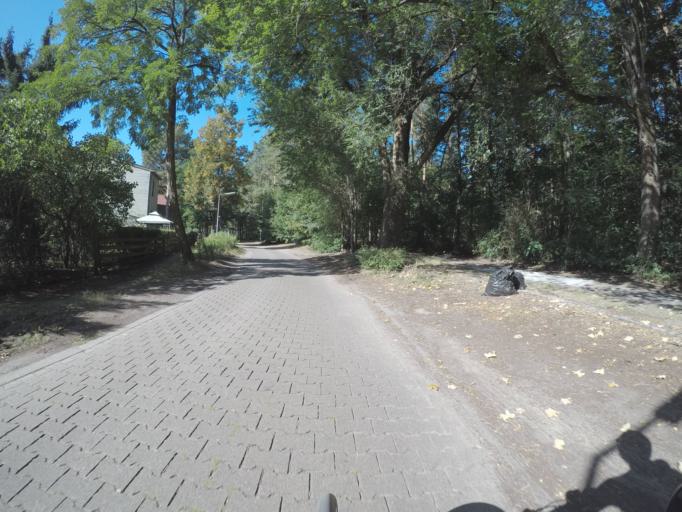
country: DE
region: Berlin
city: Konradshohe
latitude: 52.5768
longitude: 13.2255
